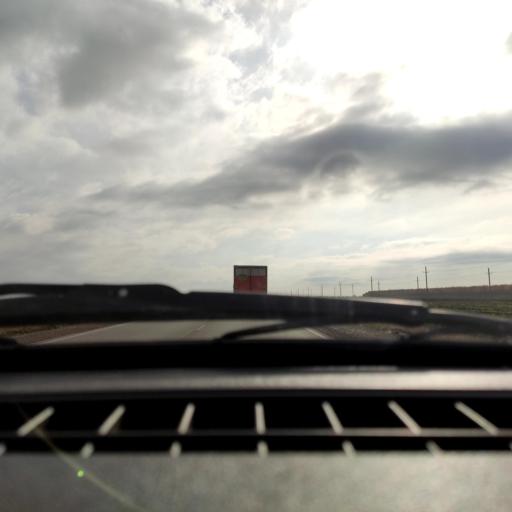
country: RU
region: Bashkortostan
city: Iglino
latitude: 54.7597
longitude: 56.2736
